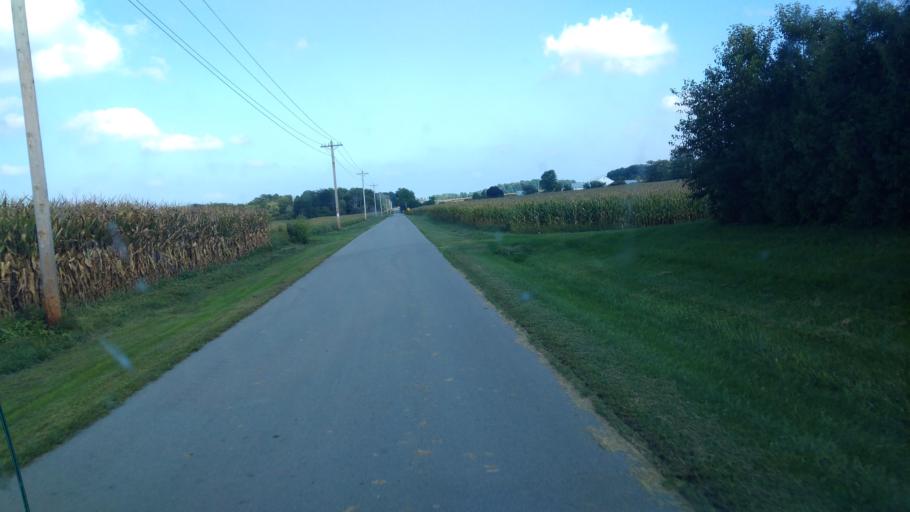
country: US
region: Ohio
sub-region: Hancock County
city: Arlington
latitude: 40.8485
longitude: -83.7126
